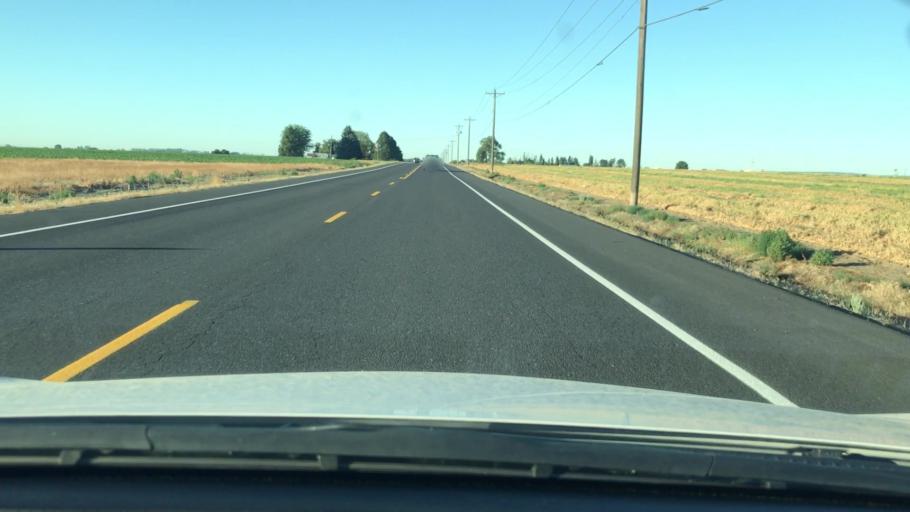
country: US
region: Washington
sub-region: Grant County
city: Moses Lake
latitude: 47.1158
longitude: -119.2360
